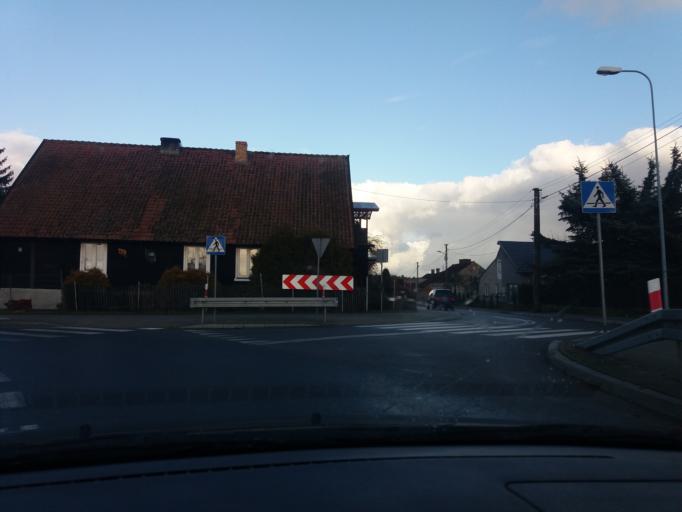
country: PL
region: Warmian-Masurian Voivodeship
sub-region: Powiat szczycienski
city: Szczytno
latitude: 53.4844
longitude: 20.9628
